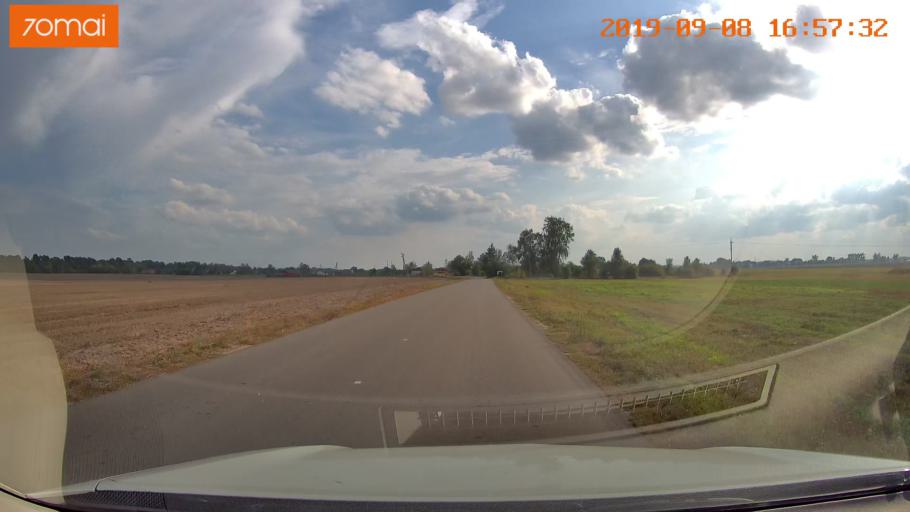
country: BY
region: Grodnenskaya
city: Hrodna
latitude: 53.7318
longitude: 23.9277
